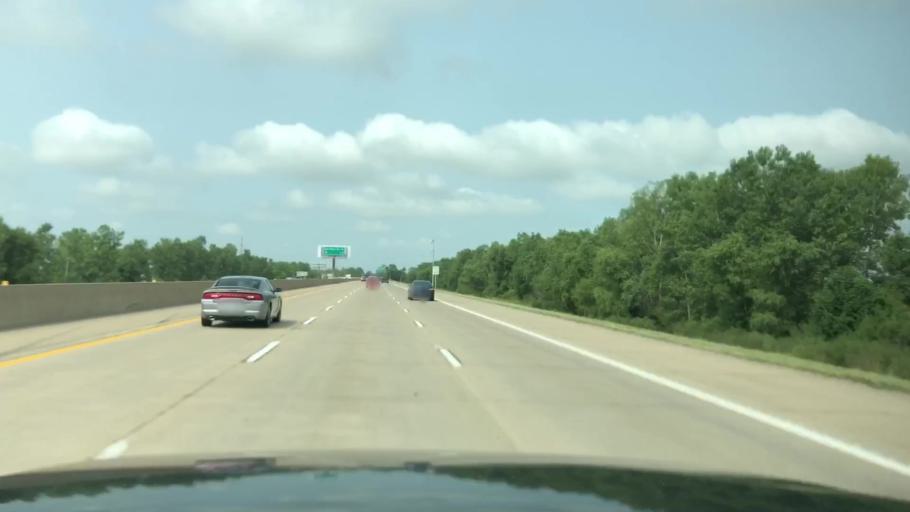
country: US
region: Missouri
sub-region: Saint Charles County
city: Saint Peters
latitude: 38.8161
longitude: -90.5715
